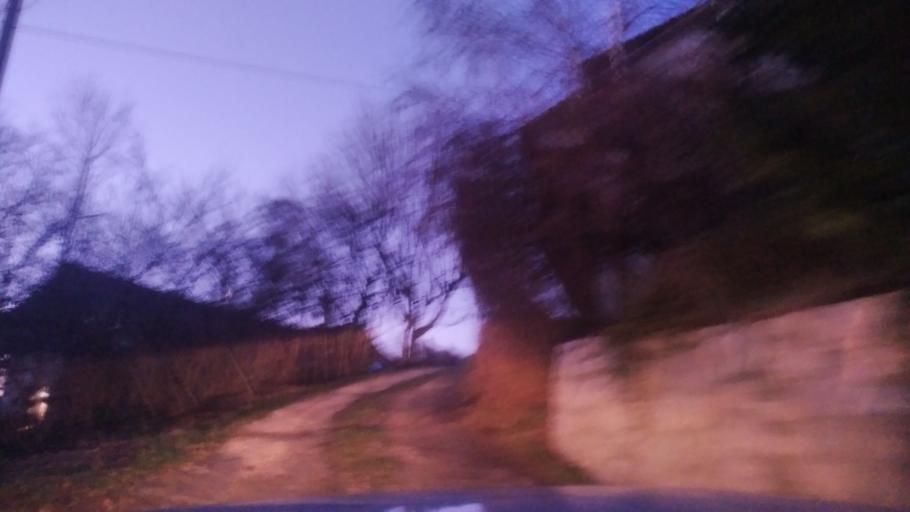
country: HU
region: Komarom-Esztergom
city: Esztergom
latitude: 47.7916
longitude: 18.7498
